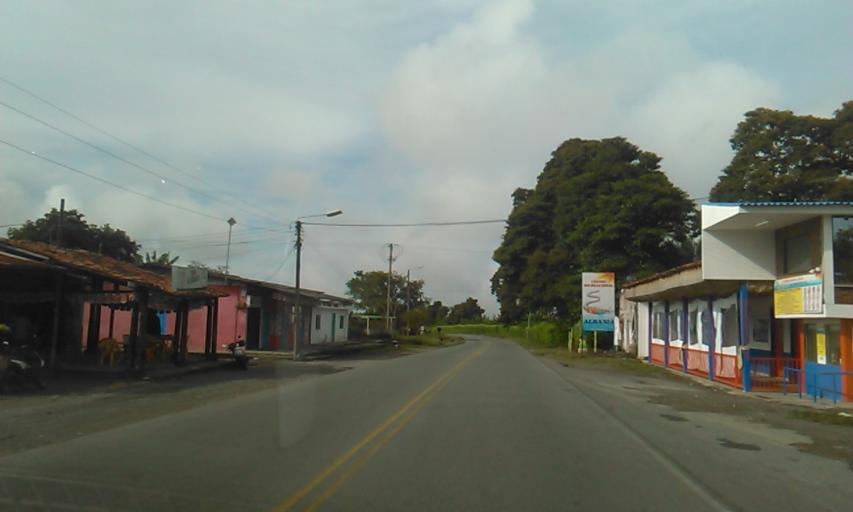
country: CO
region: Quindio
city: Cordoba
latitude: 4.4640
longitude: -75.7077
